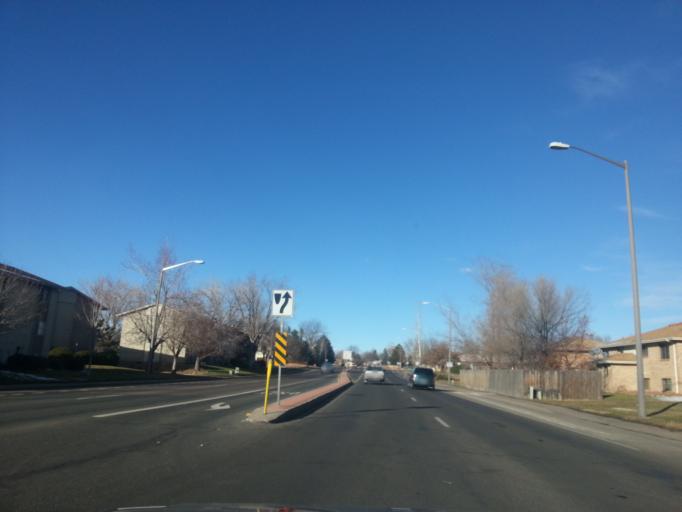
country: US
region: Colorado
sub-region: Larimer County
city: Loveland
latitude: 40.4092
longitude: -105.1103
